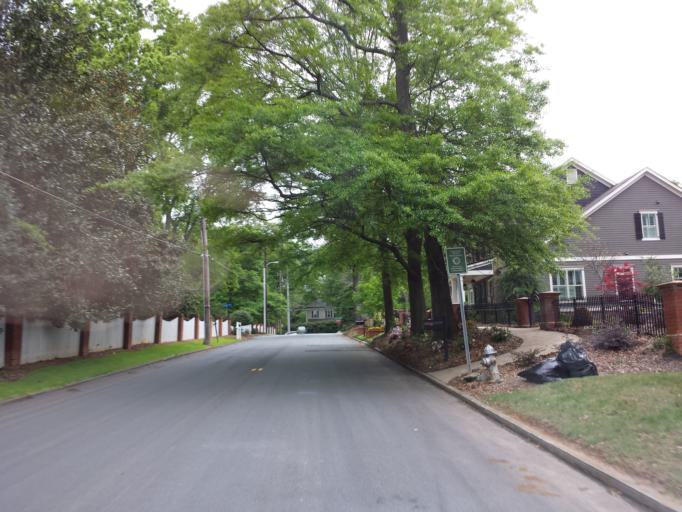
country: US
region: Georgia
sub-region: Cobb County
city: Marietta
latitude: 33.9506
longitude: -84.5612
